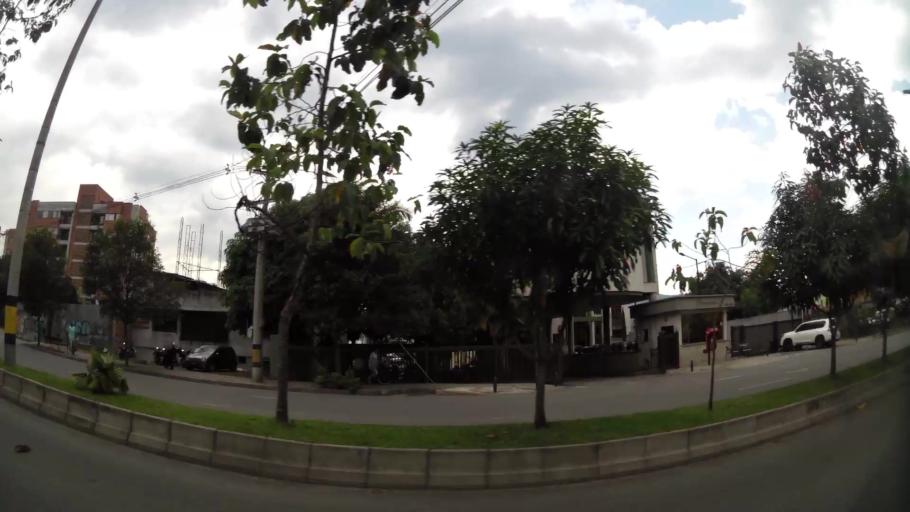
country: CO
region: Antioquia
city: Envigado
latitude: 6.1629
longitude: -75.5967
